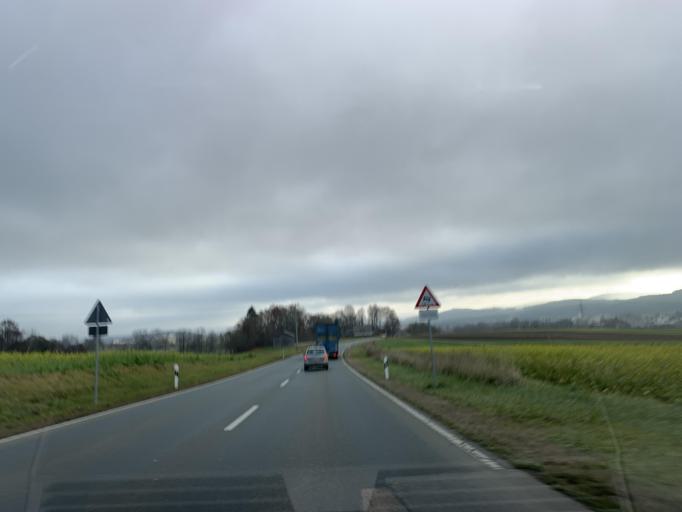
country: DE
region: Bavaria
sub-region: Upper Palatinate
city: Roetz
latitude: 49.3443
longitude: 12.5101
